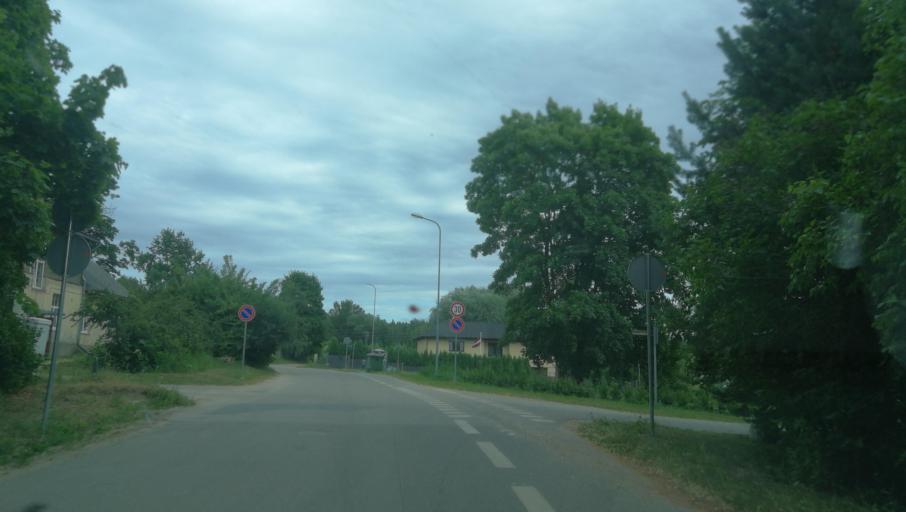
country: LV
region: Cesu Rajons
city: Cesis
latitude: 57.3000
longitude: 25.2859
